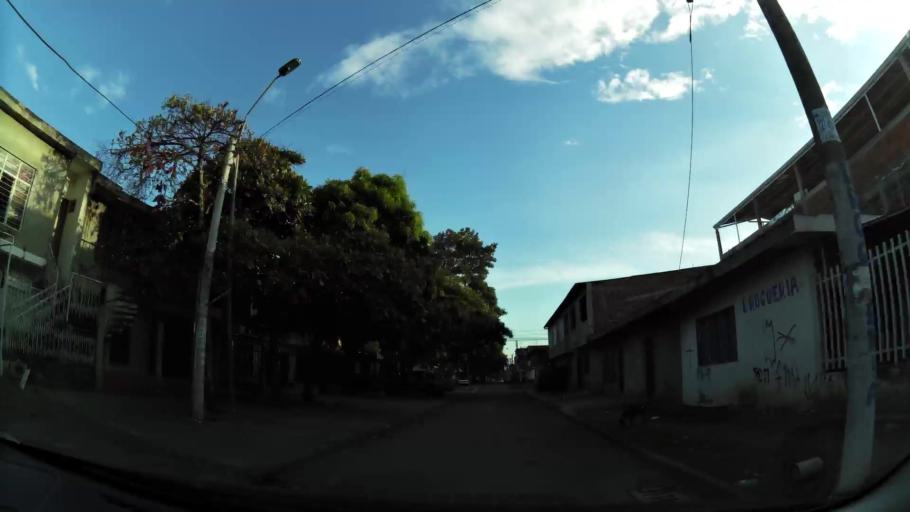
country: CO
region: Valle del Cauca
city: Cali
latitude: 3.4280
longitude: -76.5103
